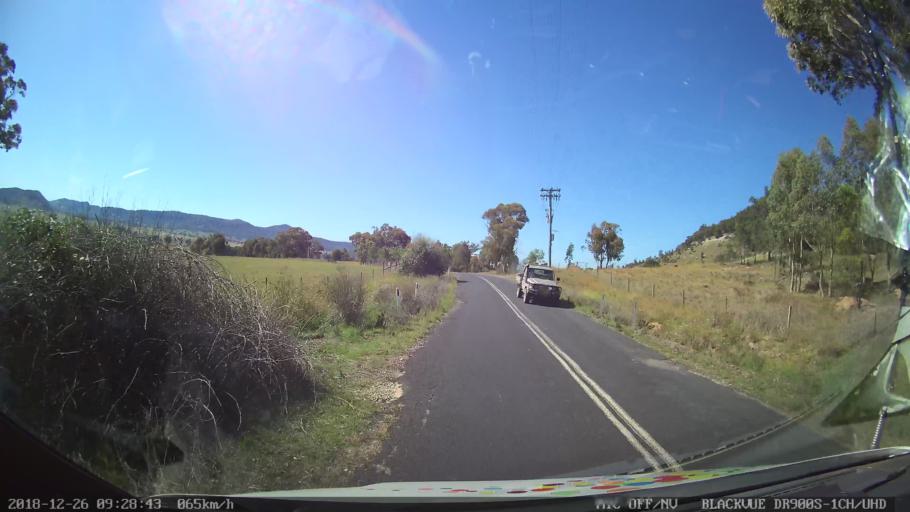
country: AU
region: New South Wales
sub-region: Mid-Western Regional
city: Kandos
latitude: -32.8471
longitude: 150.0228
